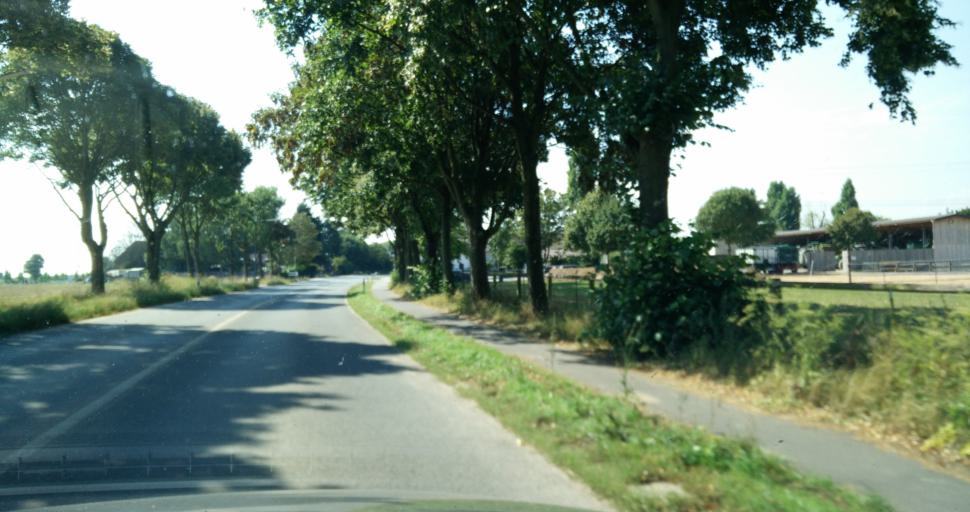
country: DE
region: North Rhine-Westphalia
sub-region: Regierungsbezirk Dusseldorf
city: Hochfeld
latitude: 51.3352
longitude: 6.7494
